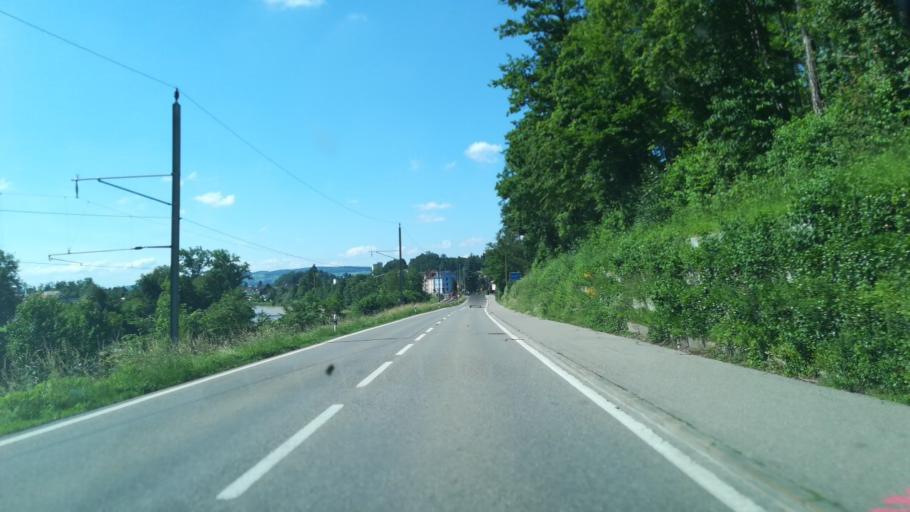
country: CH
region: Thurgau
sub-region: Weinfelden District
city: Sulgen
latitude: 47.5187
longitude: 9.2087
